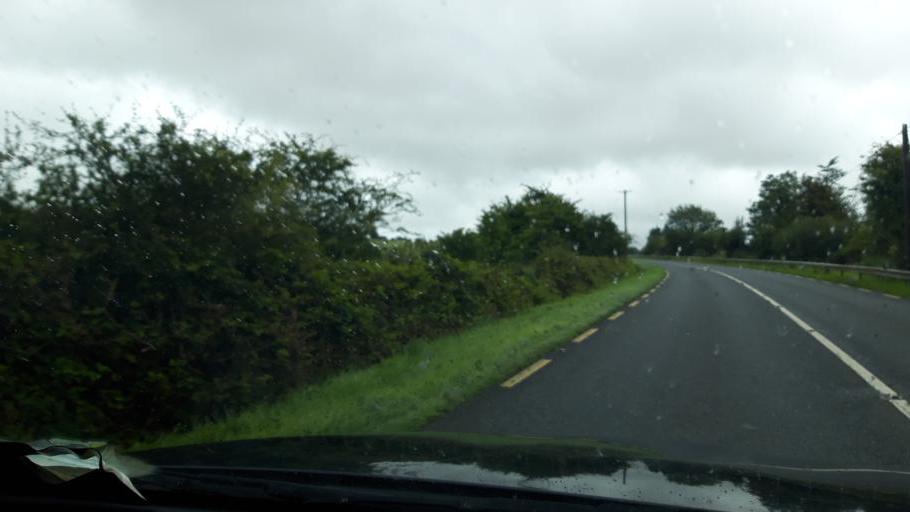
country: IE
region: Leinster
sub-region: Loch Garman
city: New Ross
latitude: 52.4293
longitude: -6.8118
